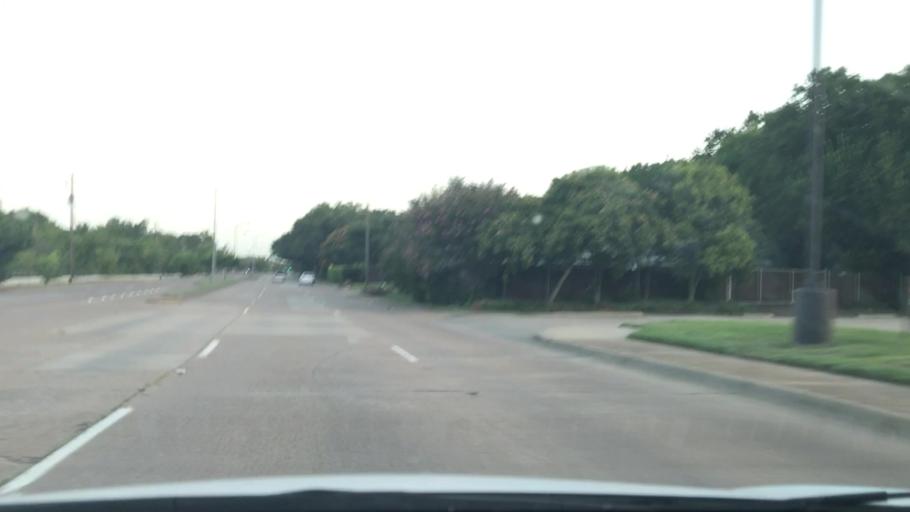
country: US
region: Texas
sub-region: Dallas County
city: Garland
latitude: 32.8705
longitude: -96.7005
